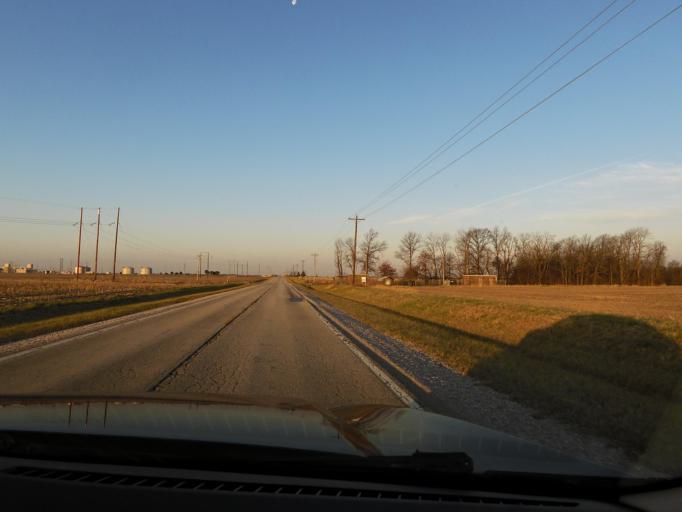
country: US
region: Illinois
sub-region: Marion County
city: Salem
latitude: 38.7651
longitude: -89.0033
